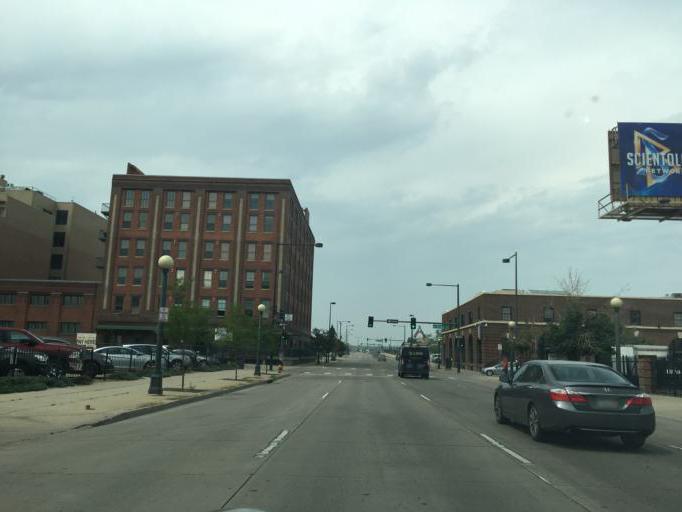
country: US
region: Colorado
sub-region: Denver County
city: Denver
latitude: 39.7567
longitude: -104.9902
